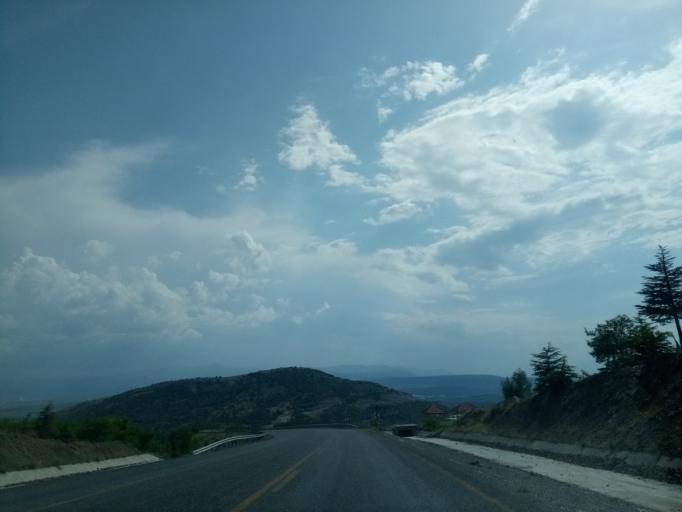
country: TR
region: Isparta
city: Bagkonak
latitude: 38.2361
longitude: 31.3141
